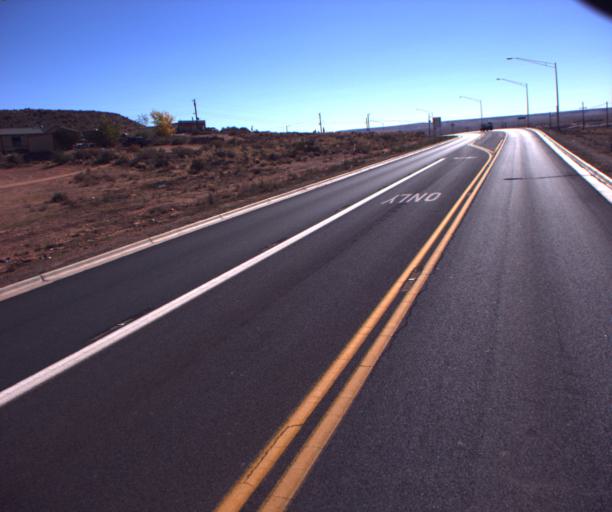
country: US
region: Arizona
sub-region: Coconino County
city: Tuba City
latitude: 36.1159
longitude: -111.2259
